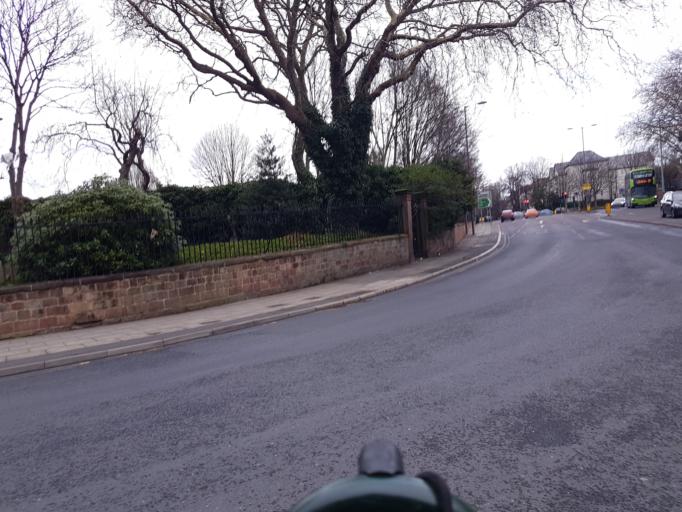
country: GB
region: England
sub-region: Liverpool
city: Liverpool
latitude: 53.3810
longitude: -2.9576
